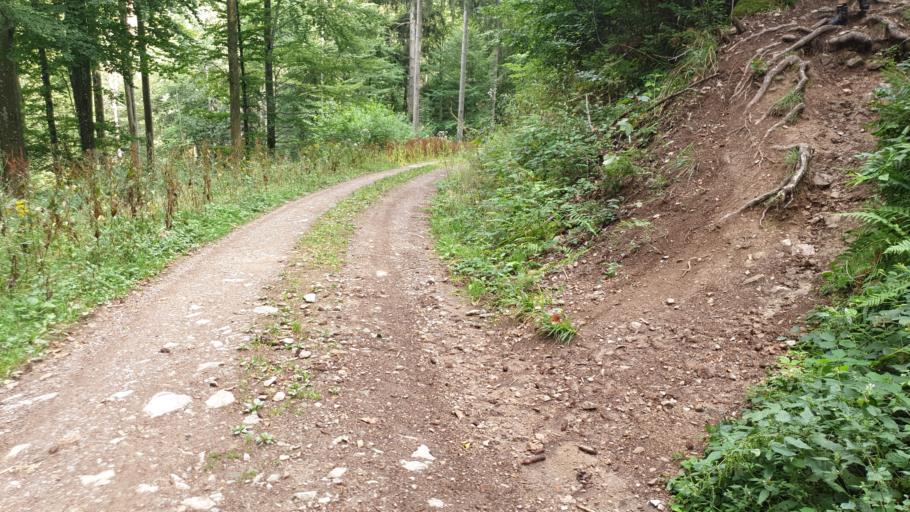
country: DE
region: Baden-Wuerttemberg
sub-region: Freiburg Region
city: Oberried
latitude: 47.9403
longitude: 7.9174
